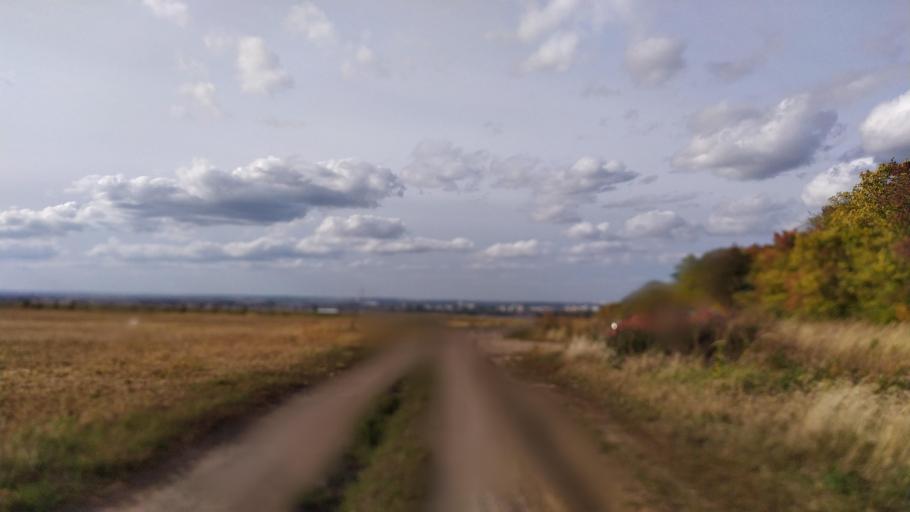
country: RU
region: Kursk
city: Kursk
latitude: 51.6126
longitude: 36.1652
